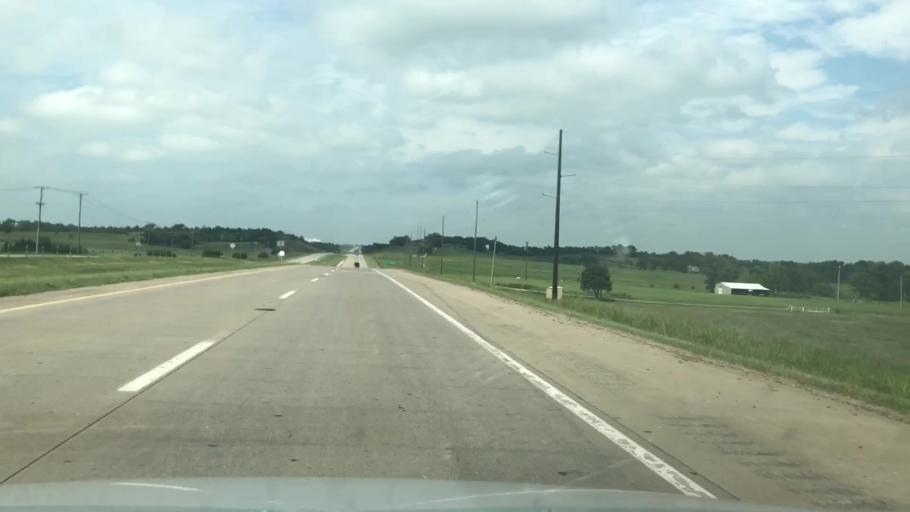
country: US
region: Oklahoma
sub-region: Osage County
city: Skiatook
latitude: 36.5384
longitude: -95.9282
